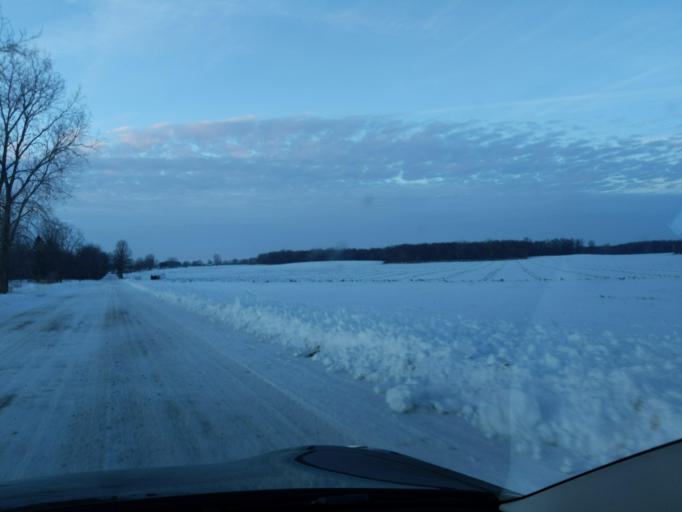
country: US
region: Michigan
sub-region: Ingham County
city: Williamston
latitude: 42.5620
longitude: -84.3059
